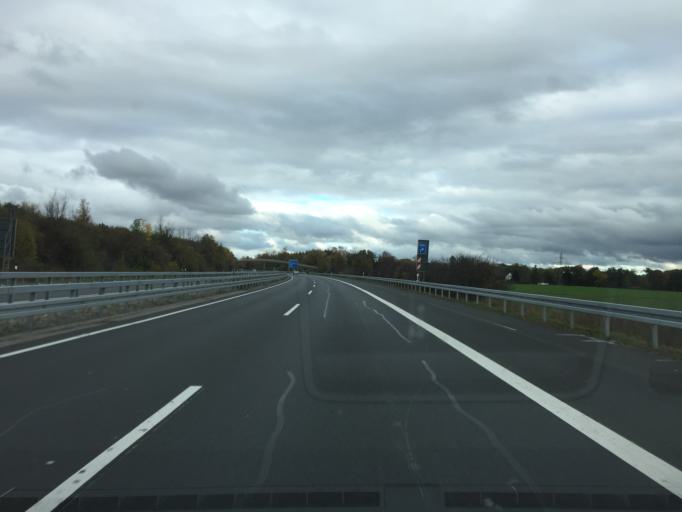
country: DE
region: Lower Saxony
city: Leiferde
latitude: 52.2054
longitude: 10.5329
